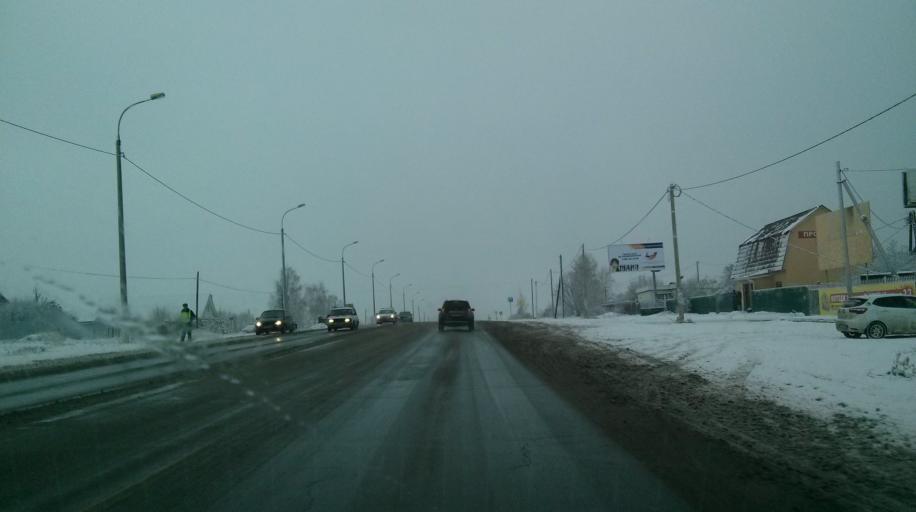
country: RU
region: Nizjnij Novgorod
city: Burevestnik
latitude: 56.1789
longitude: 43.7817
